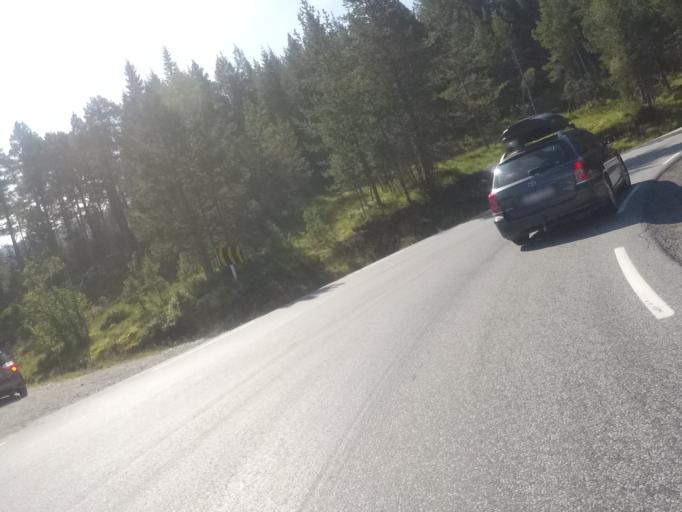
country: NO
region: Sogn og Fjordane
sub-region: Hornindal
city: Hornindal
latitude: 61.7944
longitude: 6.5330
